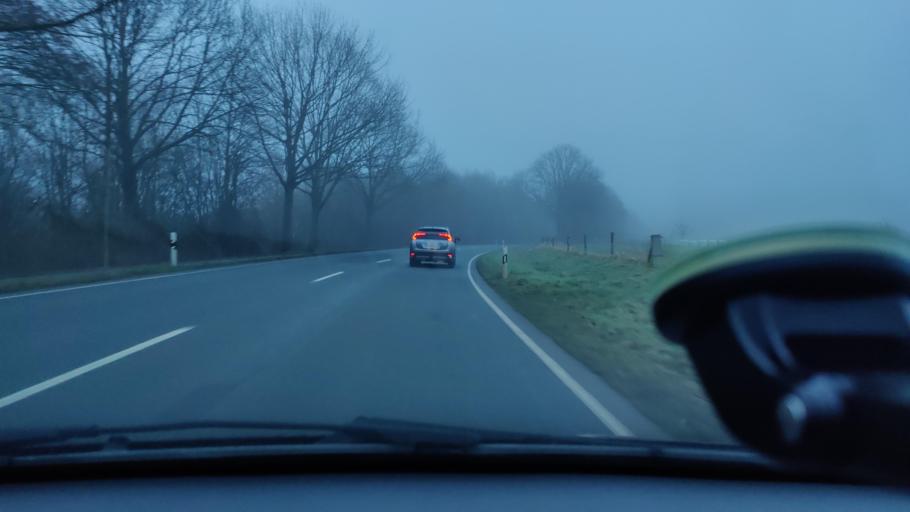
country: DE
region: North Rhine-Westphalia
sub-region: Regierungsbezirk Dusseldorf
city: Mehrhoog
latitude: 51.6854
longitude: 6.5368
